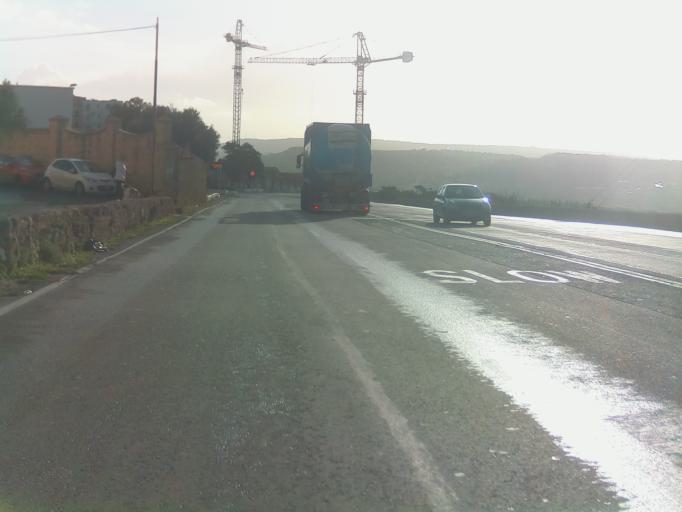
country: MT
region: Il-Mellieha
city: Mellieha
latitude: 35.9538
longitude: 14.3622
